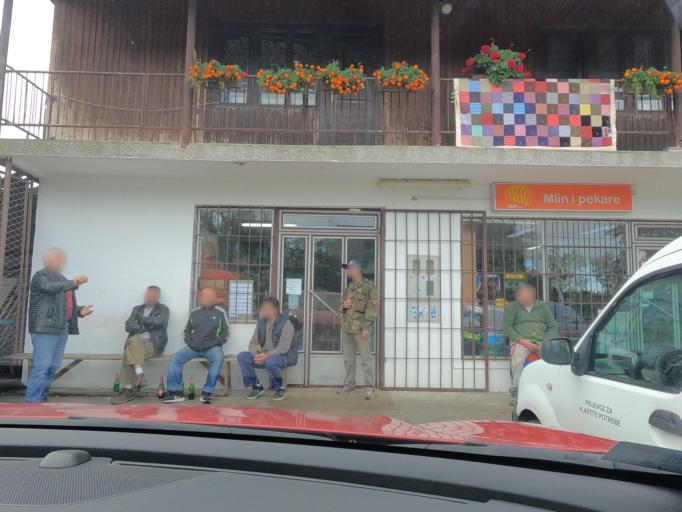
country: HR
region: Sisacko-Moslavacka
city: Petrinja
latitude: 45.3252
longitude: 16.2282
